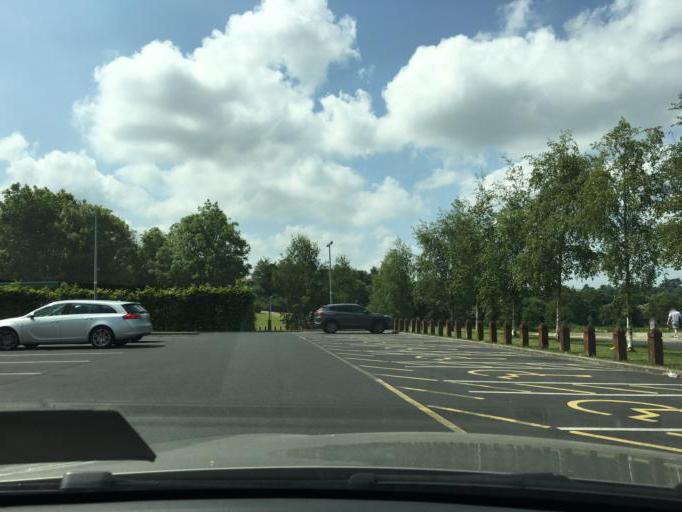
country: IE
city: Palmerstown
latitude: 53.3583
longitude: -6.3698
